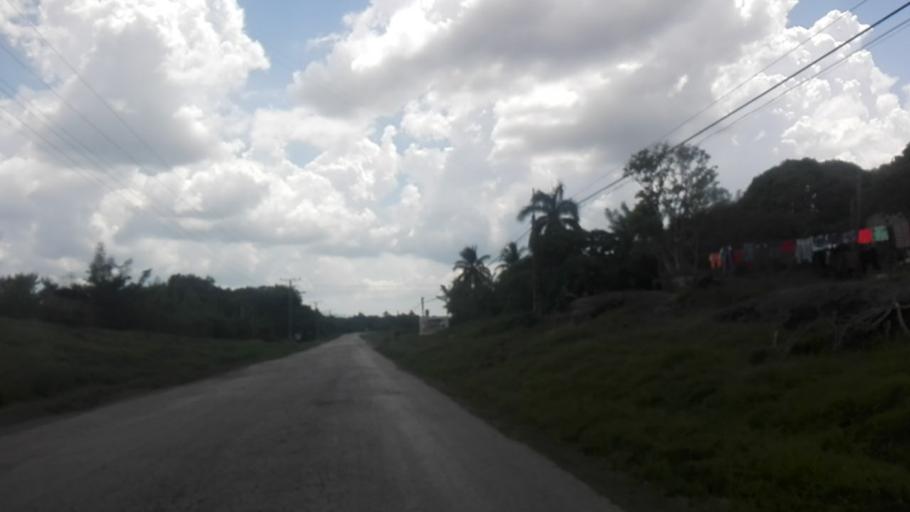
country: CU
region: Granma
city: Bartolome Maso
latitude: 20.1430
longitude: -76.9633
